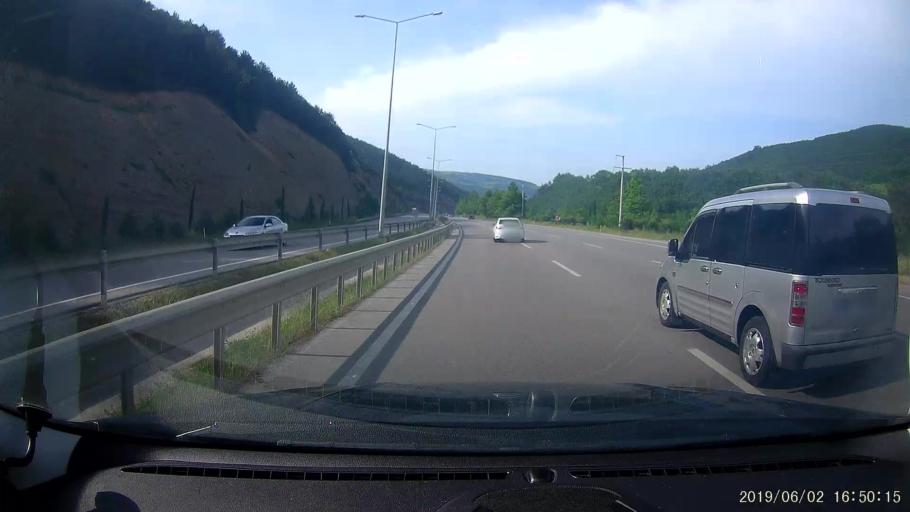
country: TR
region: Samsun
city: Samsun
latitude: 41.2511
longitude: 36.1736
